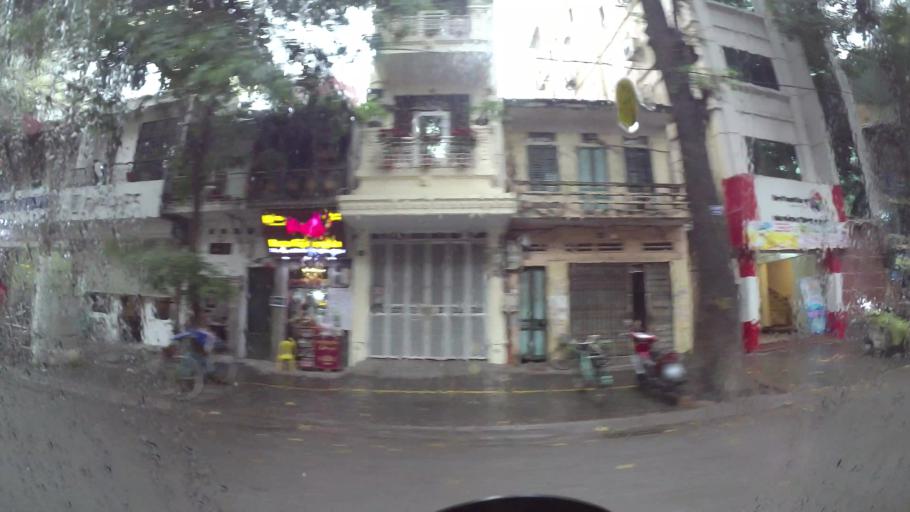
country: VN
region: Ha Noi
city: Hai BaTrung
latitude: 21.0166
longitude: 105.8560
